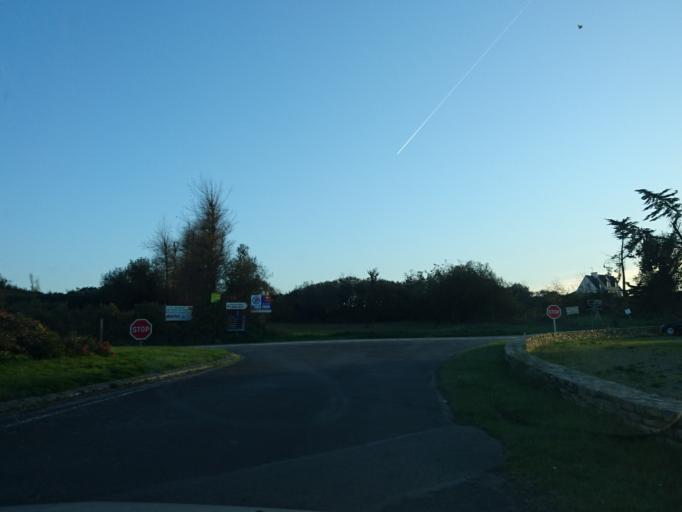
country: FR
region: Brittany
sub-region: Departement du Finistere
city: Landunvez
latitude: 48.5290
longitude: -4.7461
